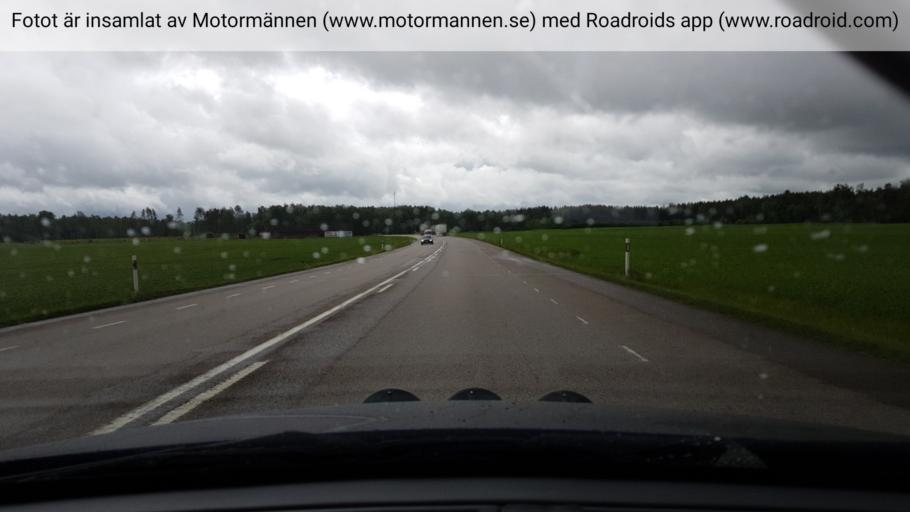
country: SE
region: Vaestra Goetaland
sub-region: Skara Kommun
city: Skara
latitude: 58.4110
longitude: 13.4651
